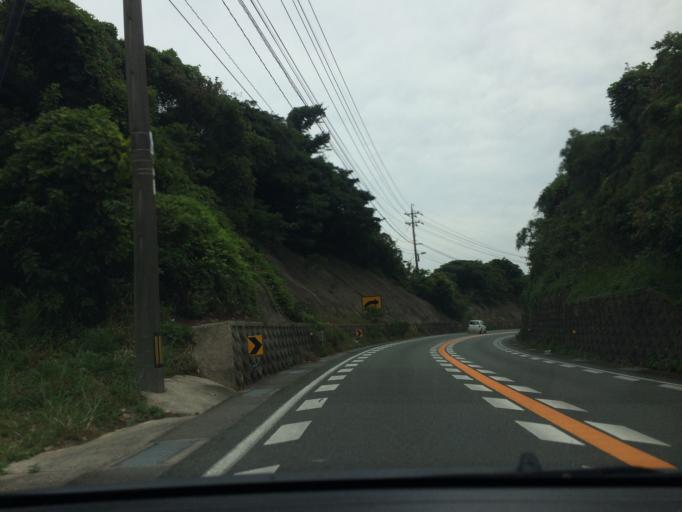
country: JP
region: Shimane
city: Gotsucho
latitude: 35.0372
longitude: 132.2578
